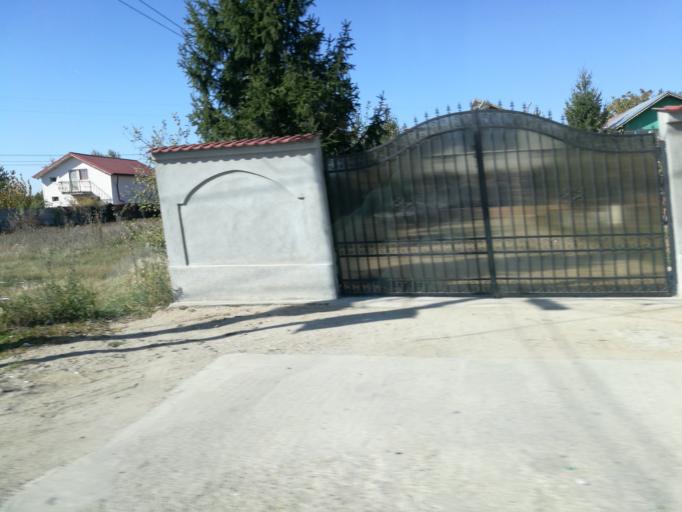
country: RO
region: Giurgiu
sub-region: Comuna Joita
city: Bacu
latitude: 44.4739
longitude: 25.8885
